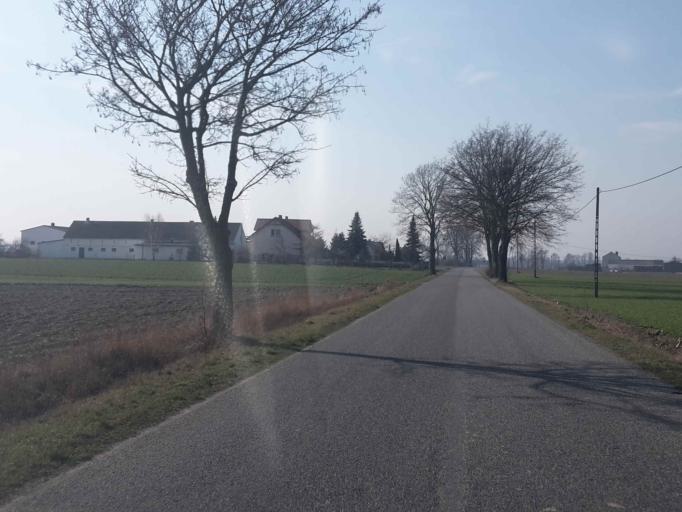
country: PL
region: Kujawsko-Pomorskie
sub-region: Powiat brodnicki
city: Bobrowo
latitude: 53.2227
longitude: 19.2478
